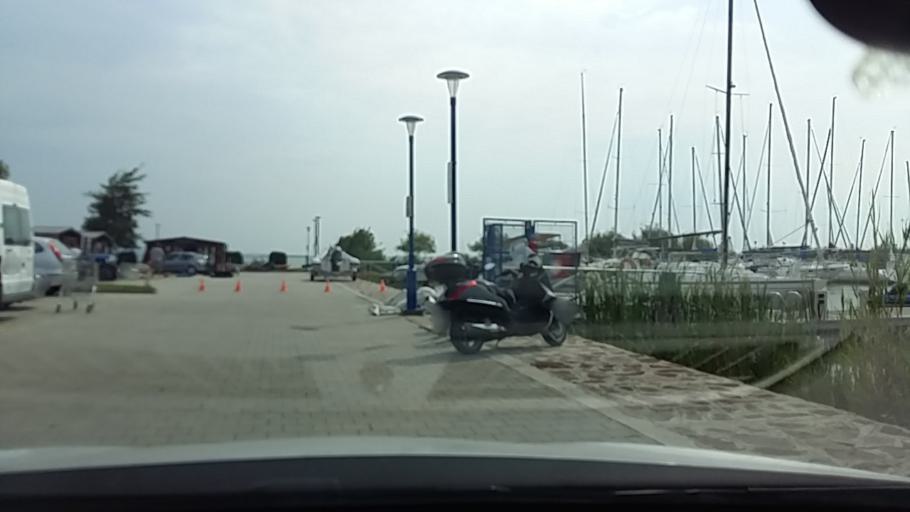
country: HU
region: Zala
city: Gyenesdias
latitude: 46.7643
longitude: 17.2658
